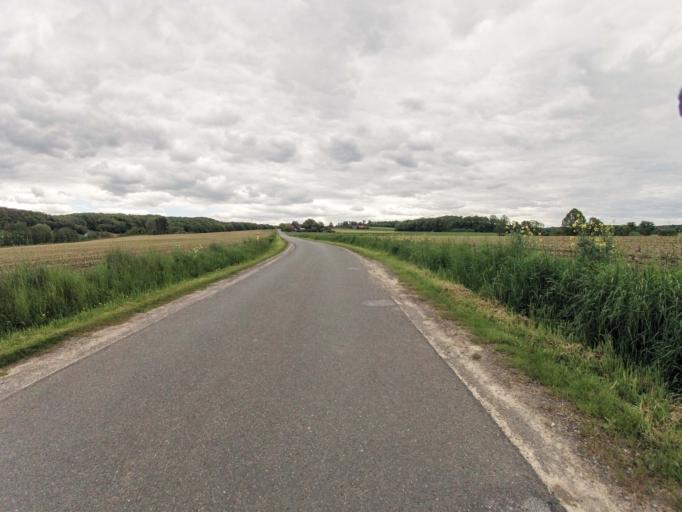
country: DE
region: Lower Saxony
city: Laar
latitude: 52.3299
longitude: 8.2682
